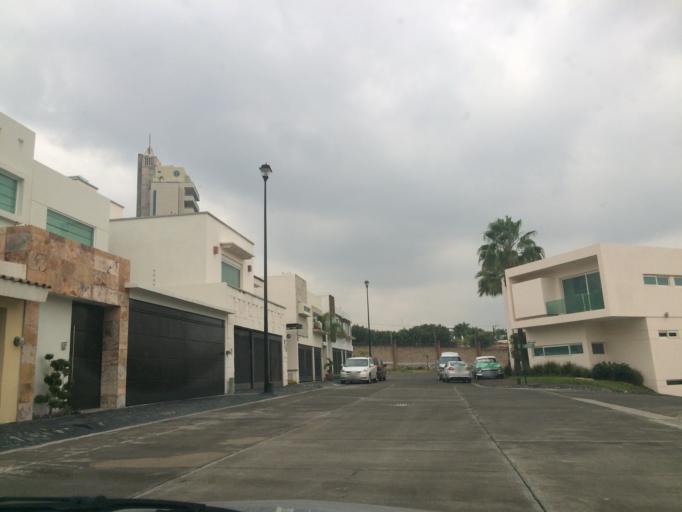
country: MX
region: Guanajuato
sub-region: Leon
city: La Ermita
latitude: 21.1733
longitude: -101.7108
